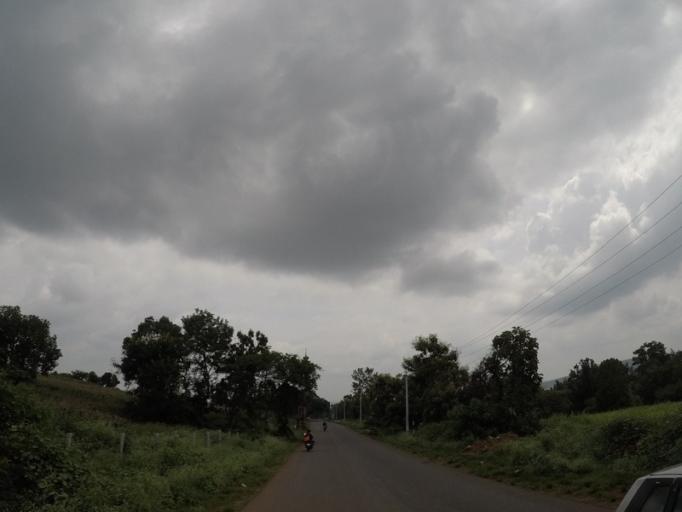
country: IN
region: Karnataka
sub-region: Chikmagalur
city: Chikmagalur
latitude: 13.3656
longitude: 75.7556
